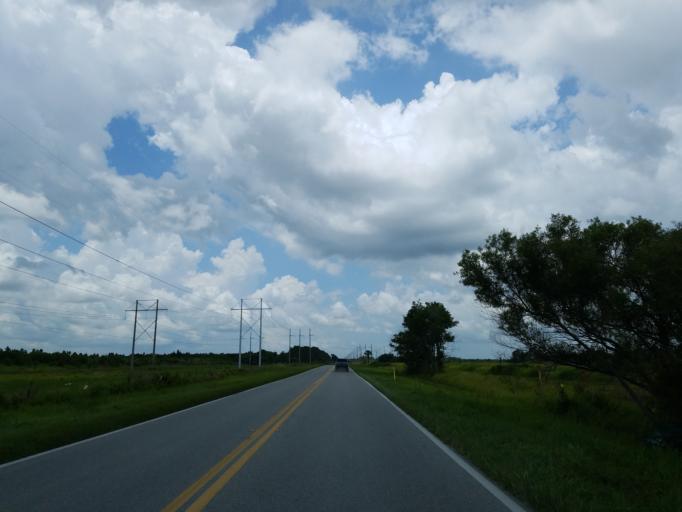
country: US
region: Florida
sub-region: Polk County
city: Willow Oak
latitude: 27.8507
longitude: -82.0331
